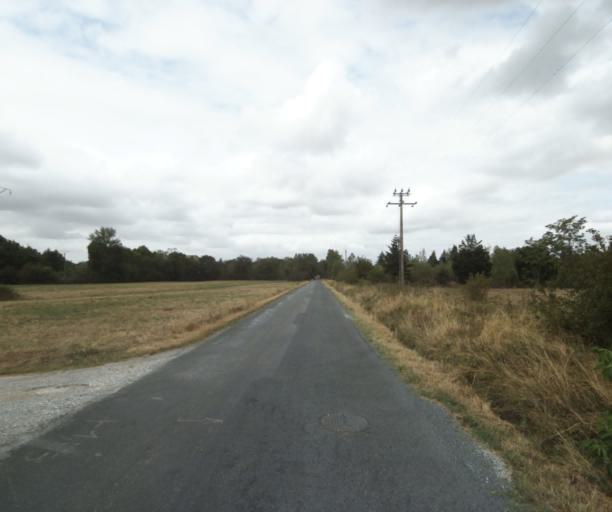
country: FR
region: Midi-Pyrenees
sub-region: Departement du Tarn
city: Soreze
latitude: 43.4478
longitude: 2.0529
